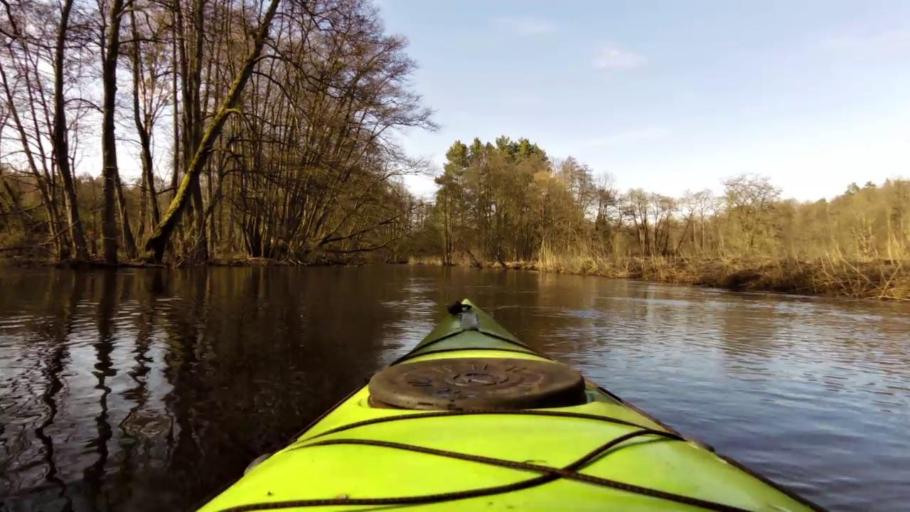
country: PL
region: West Pomeranian Voivodeship
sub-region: Powiat lobeski
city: Lobez
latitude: 53.7050
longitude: 15.5510
